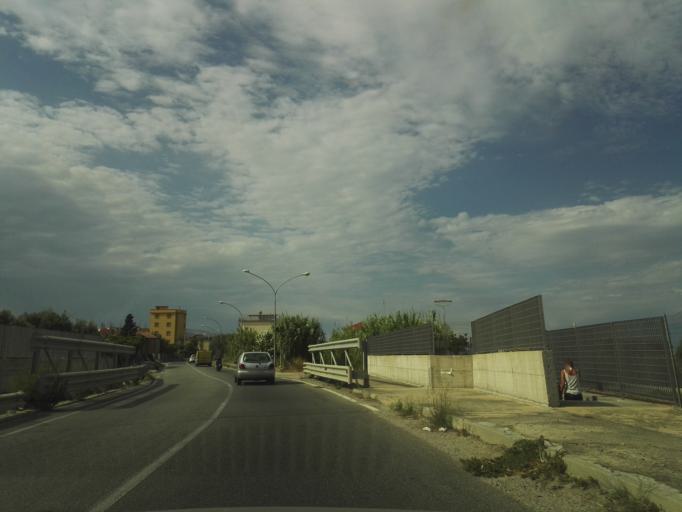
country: IT
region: Calabria
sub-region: Provincia di Catanzaro
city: Marina di Davoli
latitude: 38.6496
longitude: 16.5482
